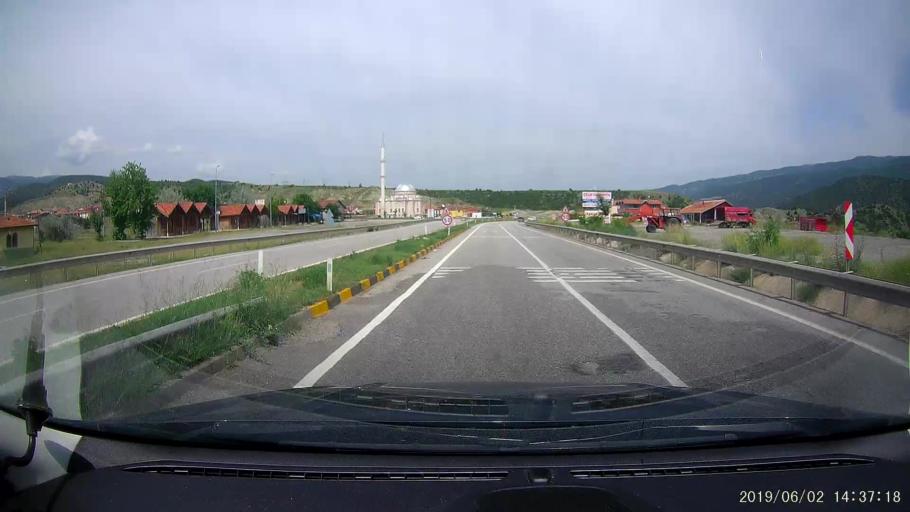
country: TR
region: Corum
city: Hacihamza
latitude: 41.0516
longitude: 34.2547
